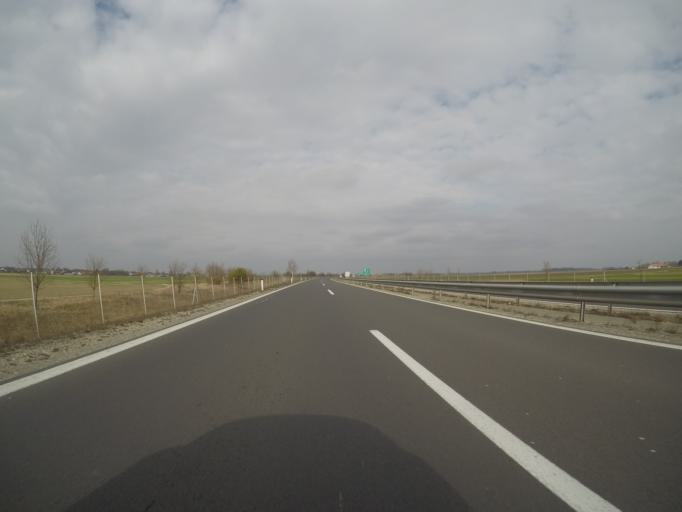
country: SI
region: Murska Sobota
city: Bakovci
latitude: 46.6235
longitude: 16.1355
